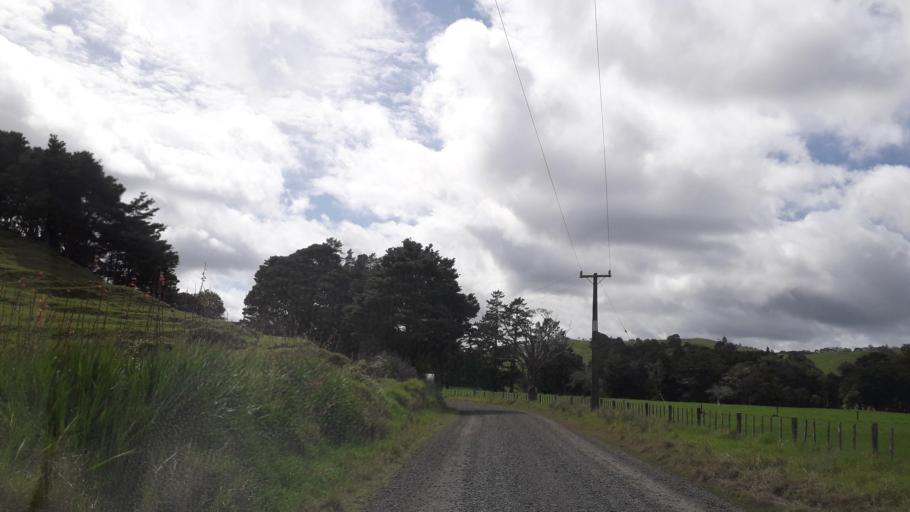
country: NZ
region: Northland
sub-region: Far North District
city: Ahipara
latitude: -35.2401
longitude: 173.2575
